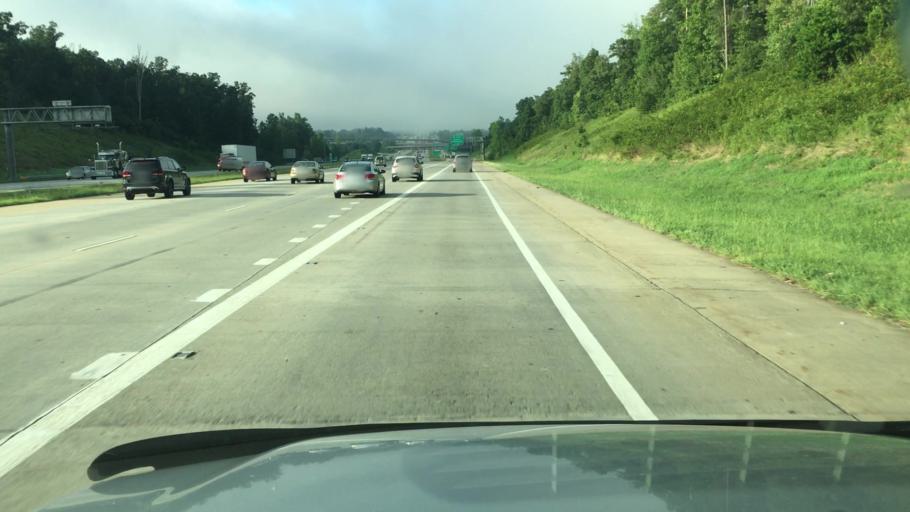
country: US
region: North Carolina
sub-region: Gaston County
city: Mount Holly
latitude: 35.2625
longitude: -80.9676
